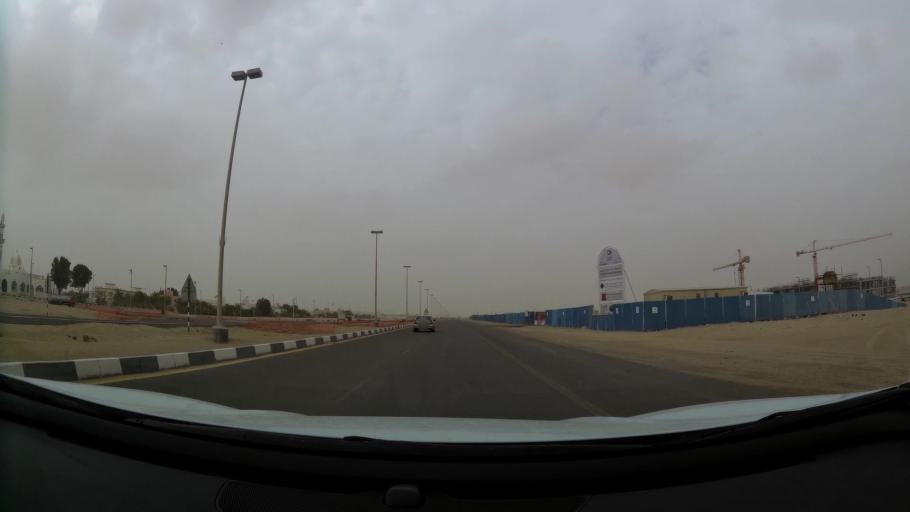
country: AE
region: Abu Dhabi
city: Abu Dhabi
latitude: 24.4290
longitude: 54.7366
